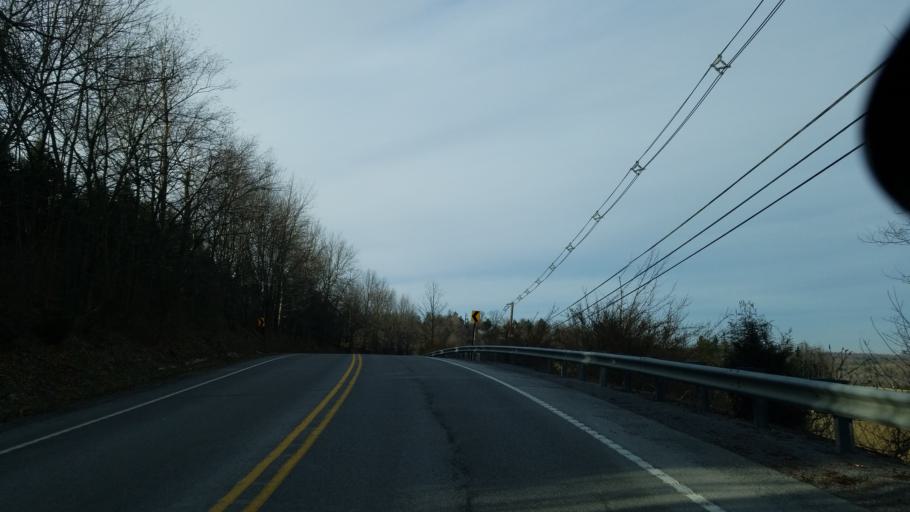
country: US
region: Pennsylvania
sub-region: Clearfield County
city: Curwensville
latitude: 40.9900
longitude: -78.6269
